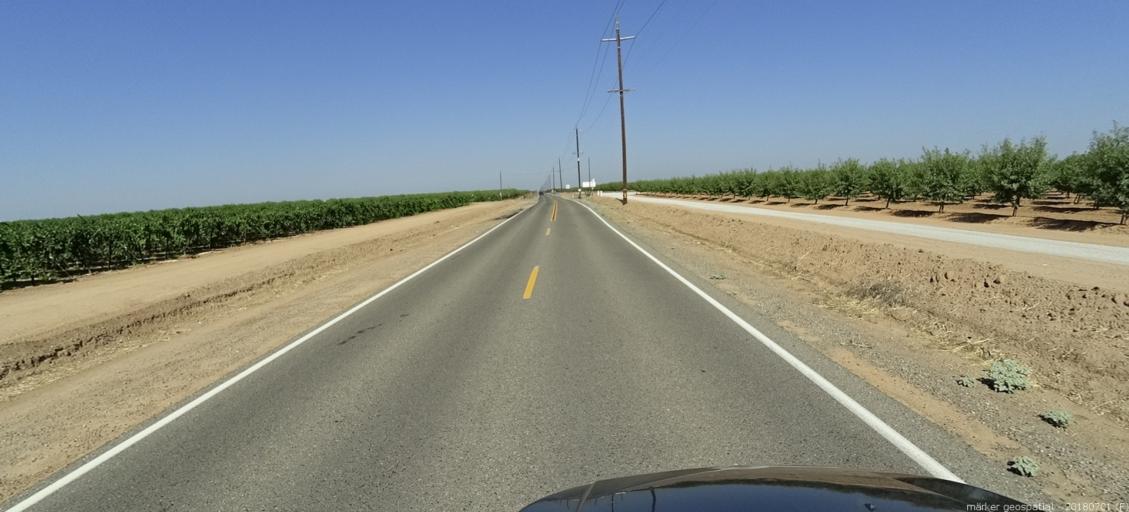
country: US
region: California
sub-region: Madera County
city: Bonadelle Ranchos-Madera Ranchos
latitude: 36.8804
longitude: -119.8376
